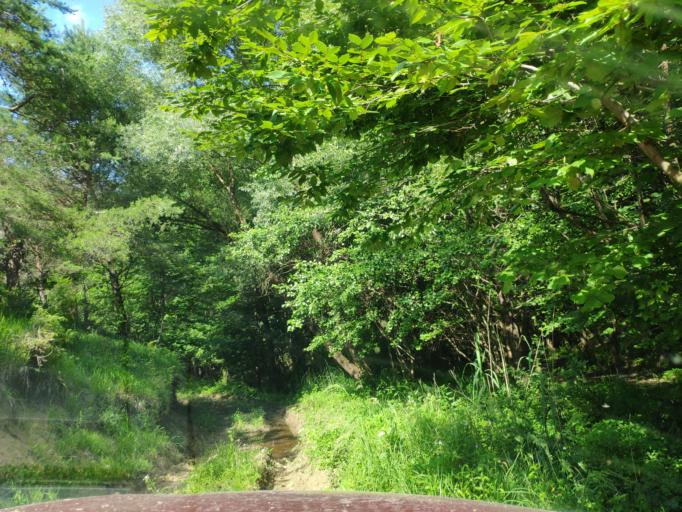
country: HU
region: Borsod-Abauj-Zemplen
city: Arlo
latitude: 48.2556
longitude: 20.1278
